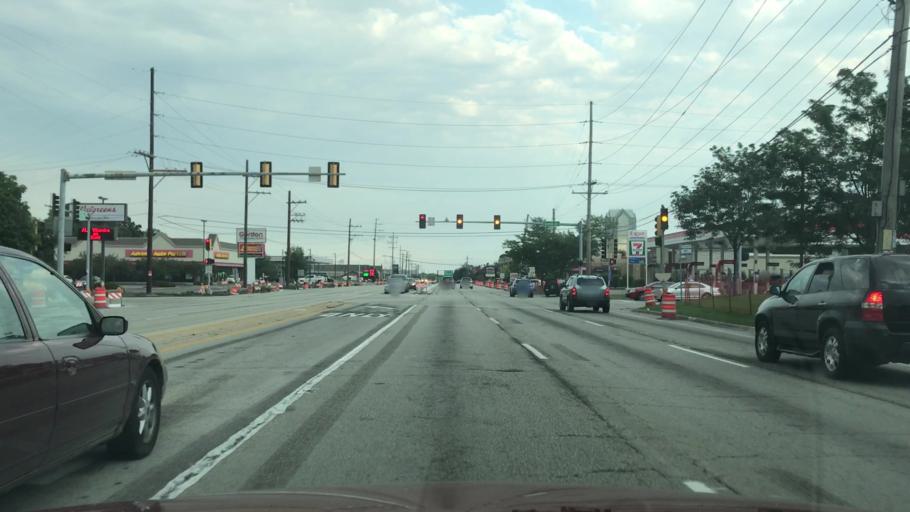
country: US
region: Illinois
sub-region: DuPage County
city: Oakbrook Terrace
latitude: 41.8605
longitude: -87.9737
